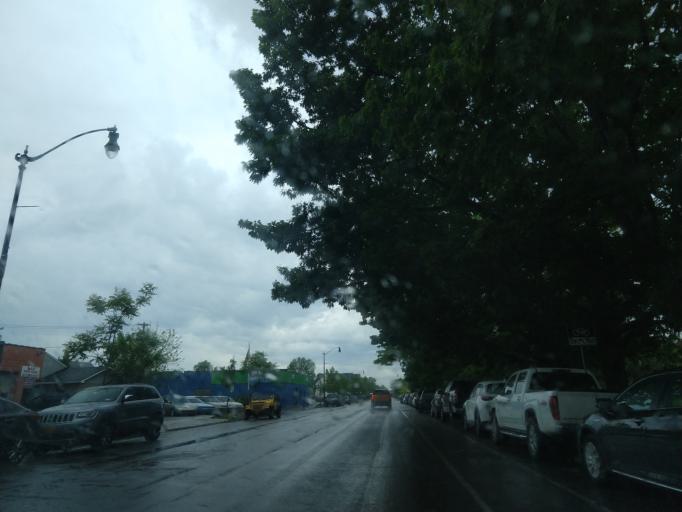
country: US
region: New York
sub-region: Erie County
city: West Seneca
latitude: 42.8524
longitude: -78.8257
